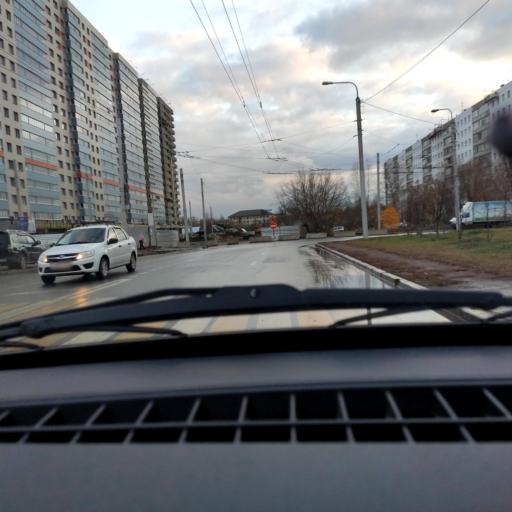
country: RU
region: Bashkortostan
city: Ufa
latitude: 54.7768
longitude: 56.1312
